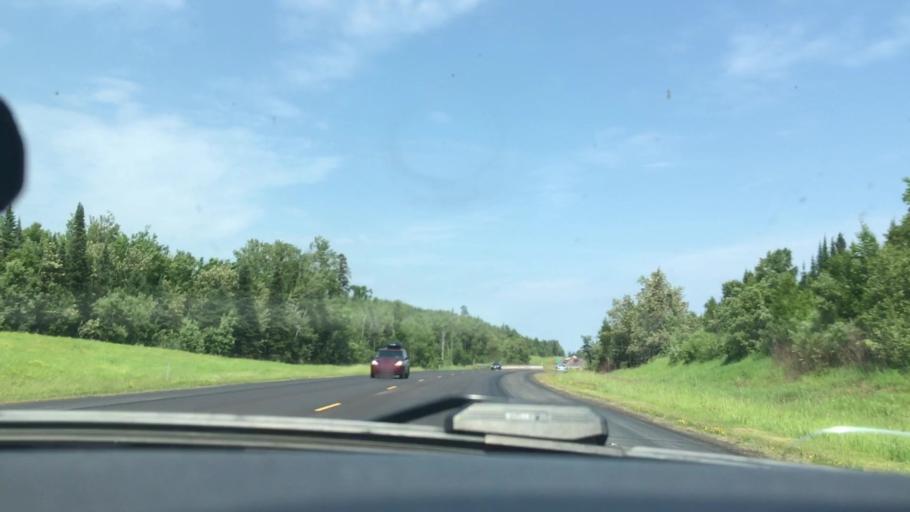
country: US
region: Minnesota
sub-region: Lake County
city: Silver Bay
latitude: 47.3356
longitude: -91.2031
